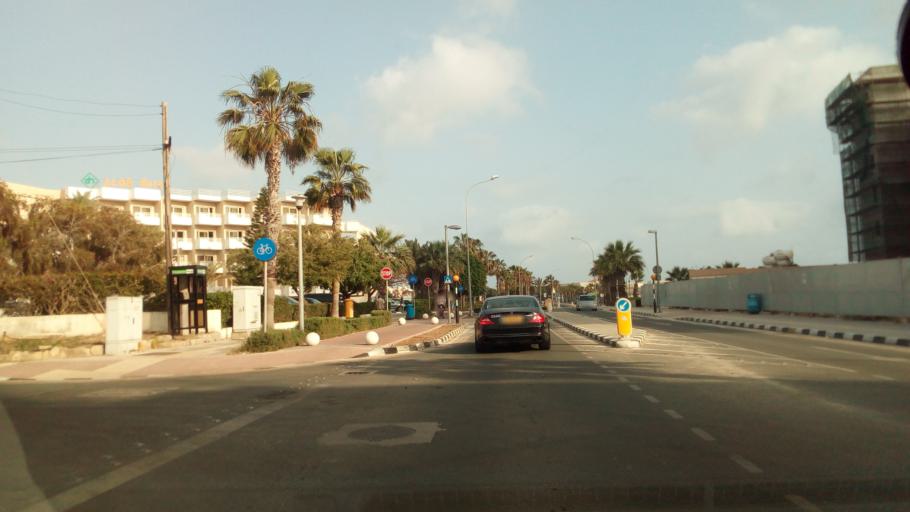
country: CY
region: Pafos
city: Paphos
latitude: 34.7511
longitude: 32.4223
